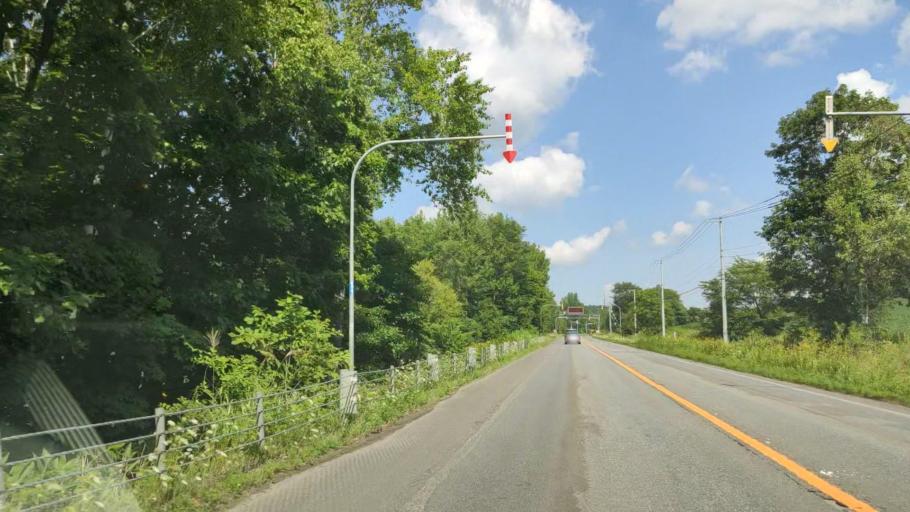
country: JP
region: Hokkaido
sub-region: Asahikawa-shi
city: Asahikawa
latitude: 43.5779
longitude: 142.4390
